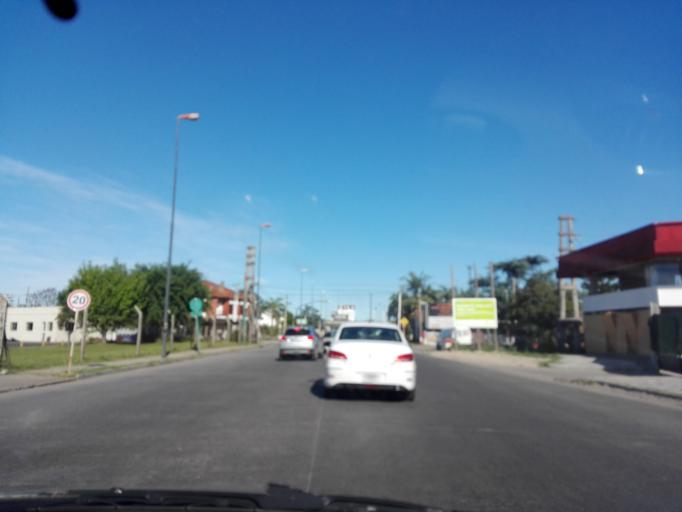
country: AR
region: Buenos Aires
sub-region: Partido de La Plata
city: La Plata
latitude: -34.8954
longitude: -57.9950
